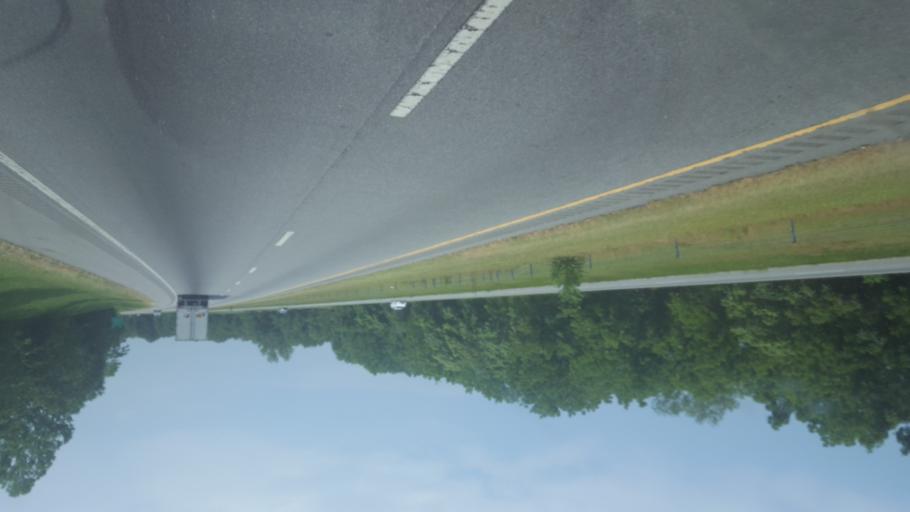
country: US
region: North Carolina
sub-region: Iredell County
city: Statesville
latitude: 35.9920
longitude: -80.8396
